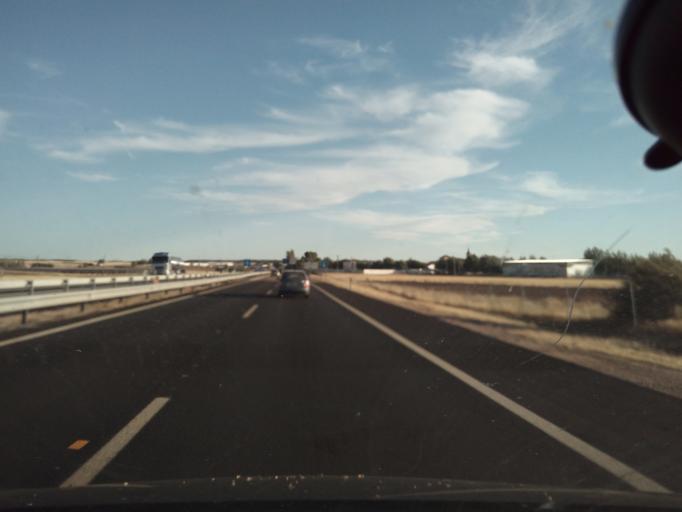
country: ES
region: Castille-La Mancha
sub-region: Province of Toledo
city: Tembleque
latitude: 39.7056
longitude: -3.4975
